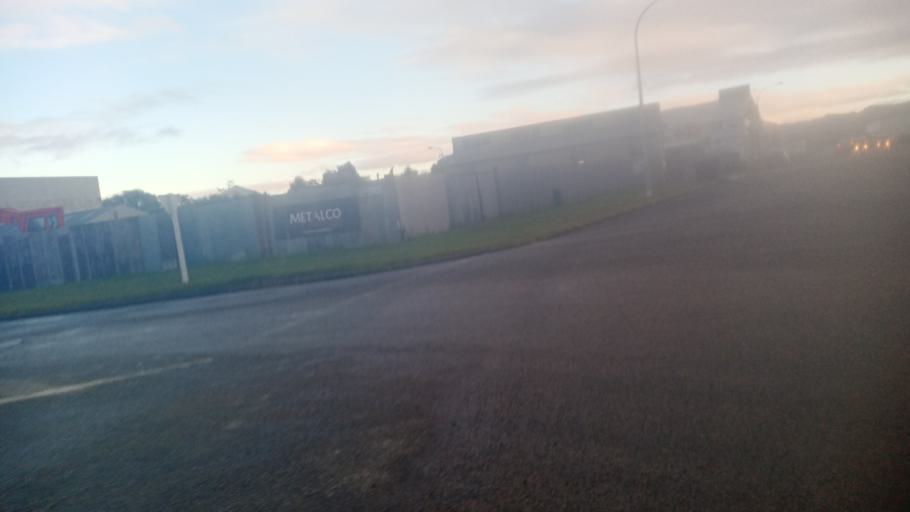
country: NZ
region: Gisborne
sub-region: Gisborne District
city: Gisborne
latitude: -38.6674
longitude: 178.0018
